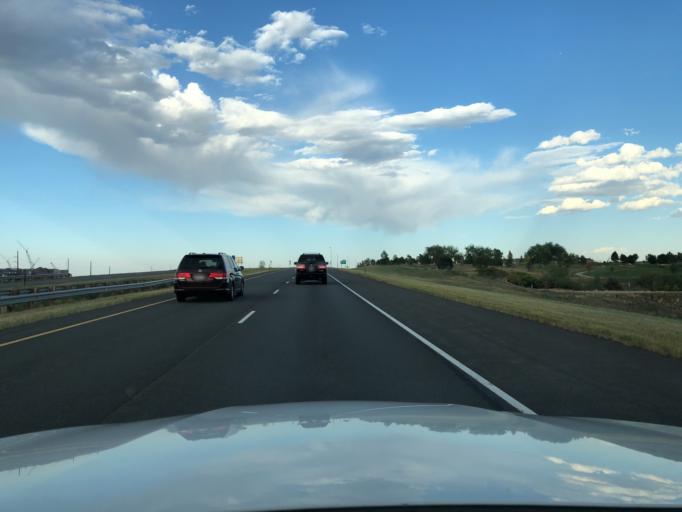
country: US
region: Colorado
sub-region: Boulder County
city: Lafayette
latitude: 39.9823
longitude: -105.0310
